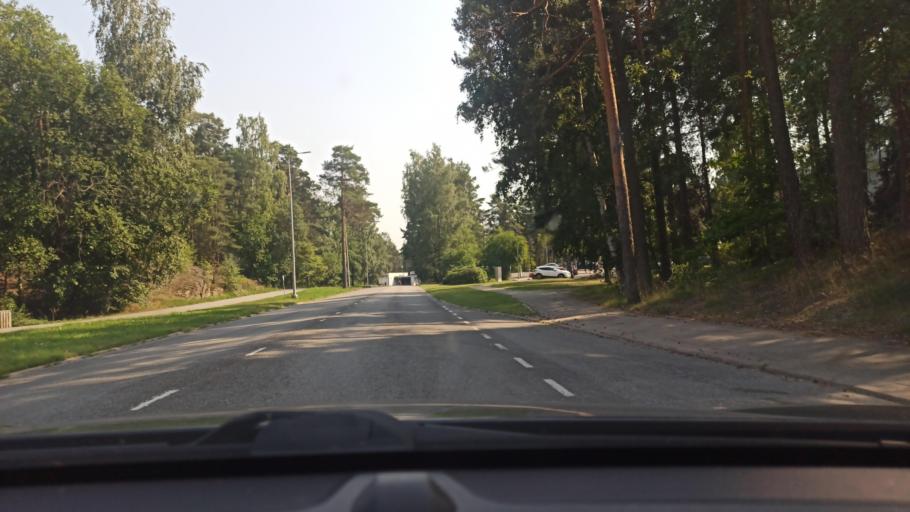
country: FI
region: Varsinais-Suomi
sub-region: Turku
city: Turku
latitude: 60.4628
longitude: 22.2176
